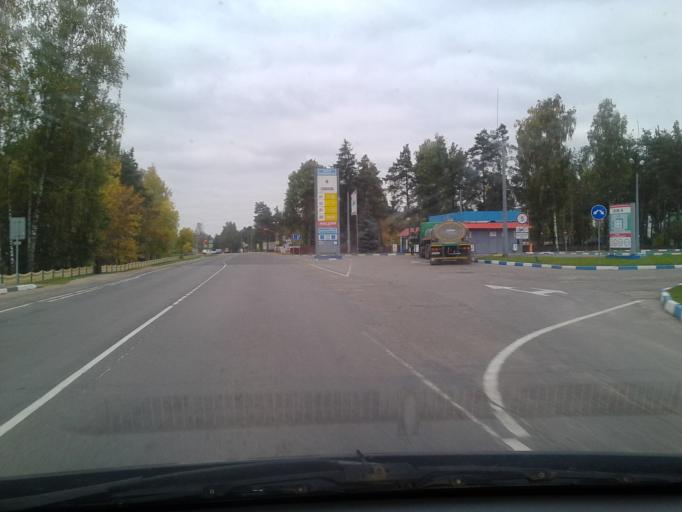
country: BY
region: Vitebsk
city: Pastavy
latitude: 55.1108
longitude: 26.8730
